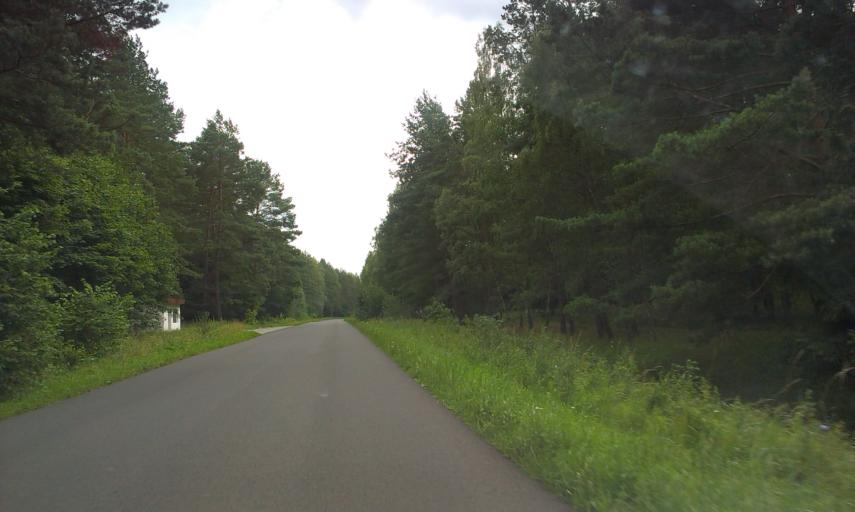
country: PL
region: Greater Poland Voivodeship
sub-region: Powiat zlotowski
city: Zlotow
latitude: 53.4837
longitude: 16.9925
